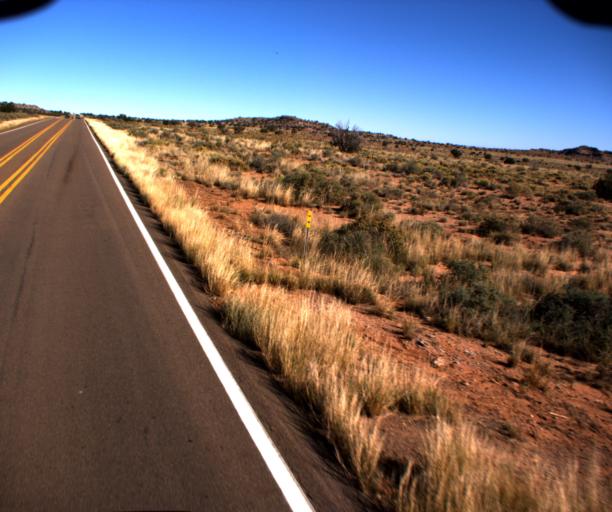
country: US
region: Arizona
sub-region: Navajo County
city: Snowflake
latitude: 34.6750
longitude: -110.1027
